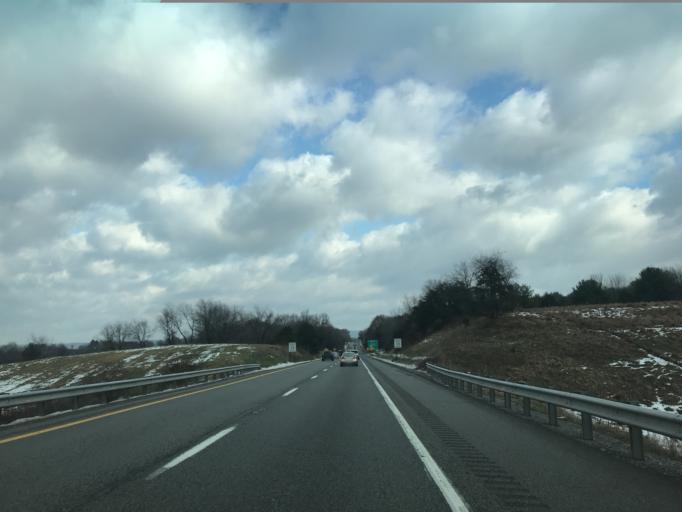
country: US
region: Pennsylvania
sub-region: Bedford County
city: Earlston
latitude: 39.9864
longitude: -78.2427
